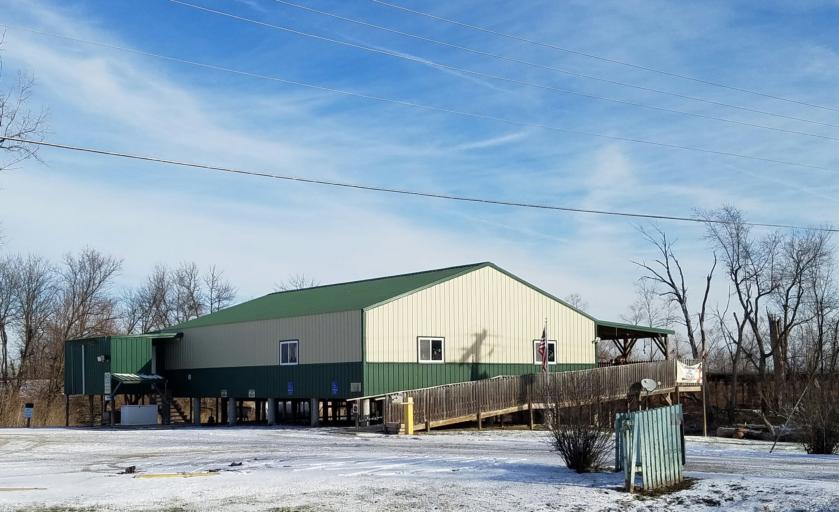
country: US
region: Missouri
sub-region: Lafayette County
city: Lexington
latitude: 39.1344
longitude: -93.9809
